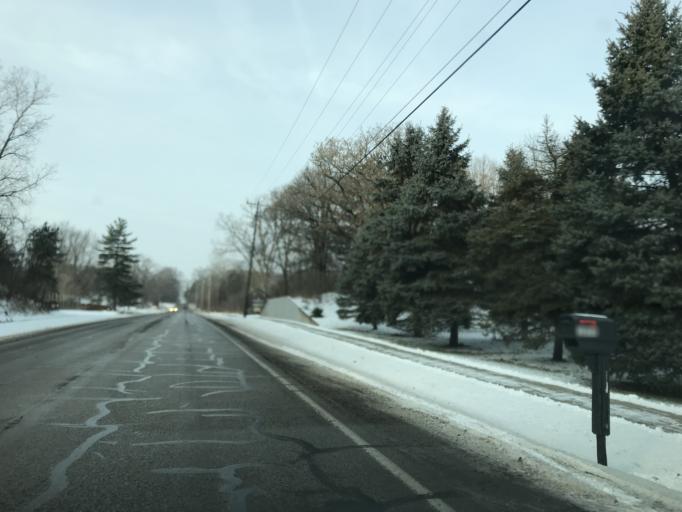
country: US
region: Michigan
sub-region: Kent County
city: Byron Center
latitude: 42.7252
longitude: -85.7312
